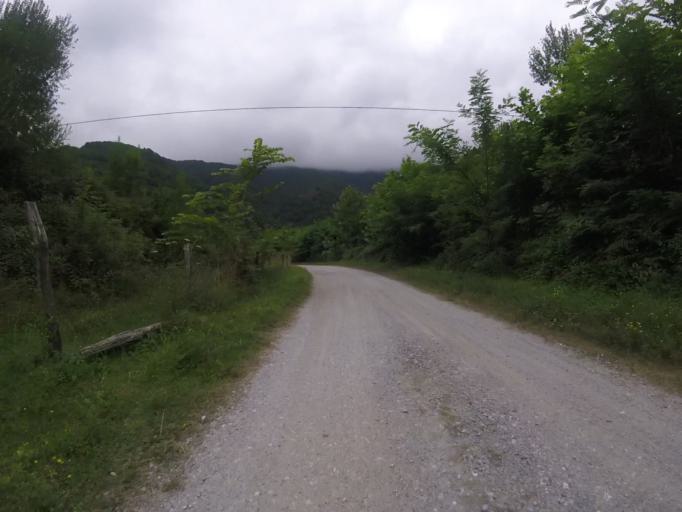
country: ES
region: Navarre
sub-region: Provincia de Navarra
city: Sunbilla
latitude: 43.1946
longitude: -1.6664
